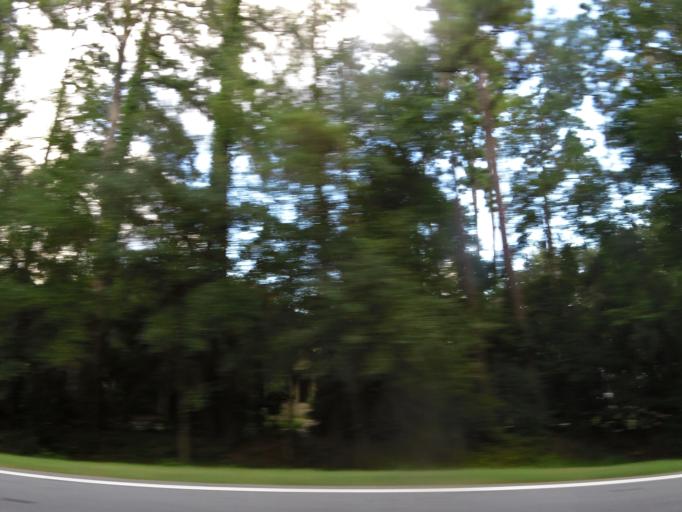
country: US
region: Georgia
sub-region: Glynn County
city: Saint Simon Mills
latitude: 31.1718
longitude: -81.4019
